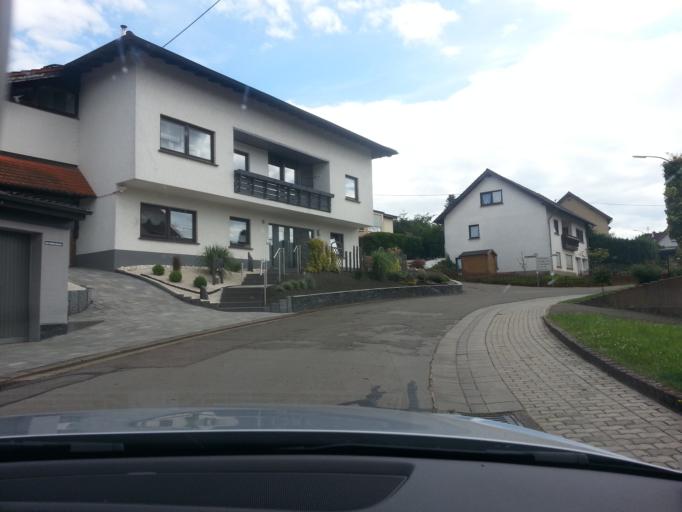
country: DE
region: Saarland
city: Marpingen
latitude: 49.4309
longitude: 7.0288
